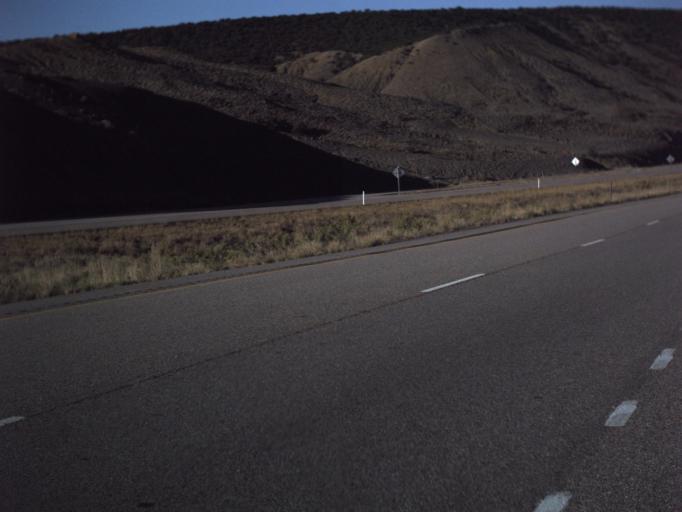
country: US
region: Utah
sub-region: Emery County
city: Ferron
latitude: 38.7679
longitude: -111.3432
